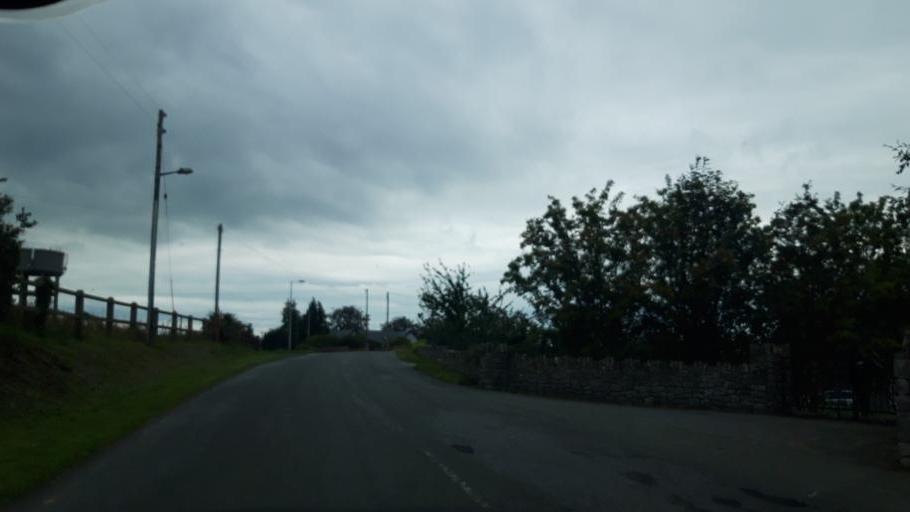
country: IE
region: Leinster
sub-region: Kilkenny
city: Ballyragget
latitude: 52.7917
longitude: -7.3373
